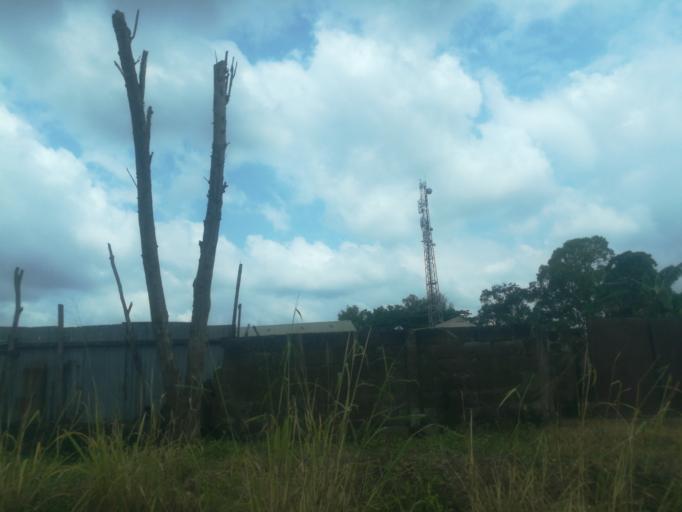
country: NG
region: Oyo
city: Ibadan
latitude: 7.3610
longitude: 3.8452
